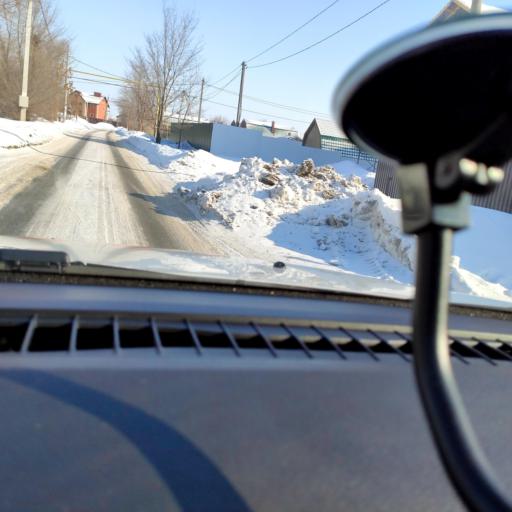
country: RU
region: Samara
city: Samara
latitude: 53.1370
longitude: 50.2428
